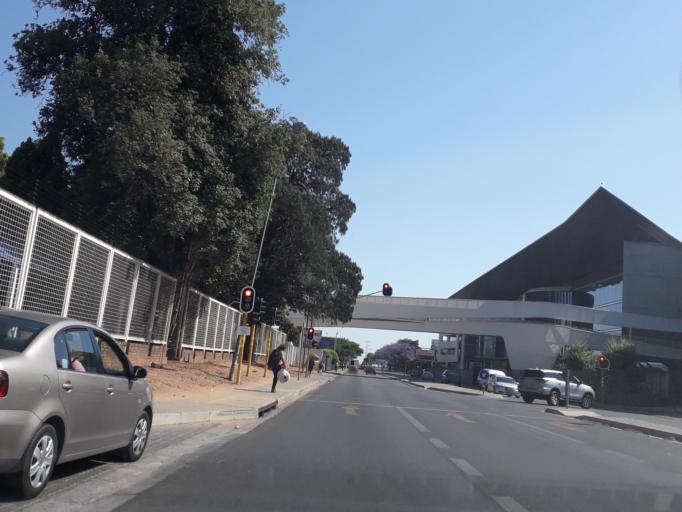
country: ZA
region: Gauteng
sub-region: City of Johannesburg Metropolitan Municipality
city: Johannesburg
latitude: -26.1025
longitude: 28.0023
